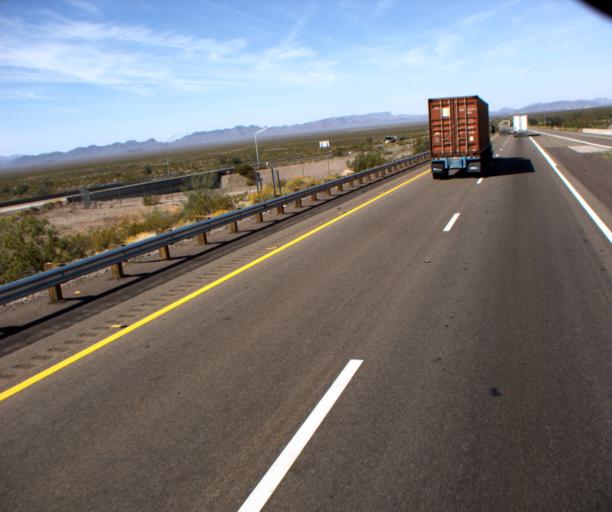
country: US
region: Arizona
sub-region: La Paz County
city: Salome
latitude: 33.6136
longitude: -113.6482
